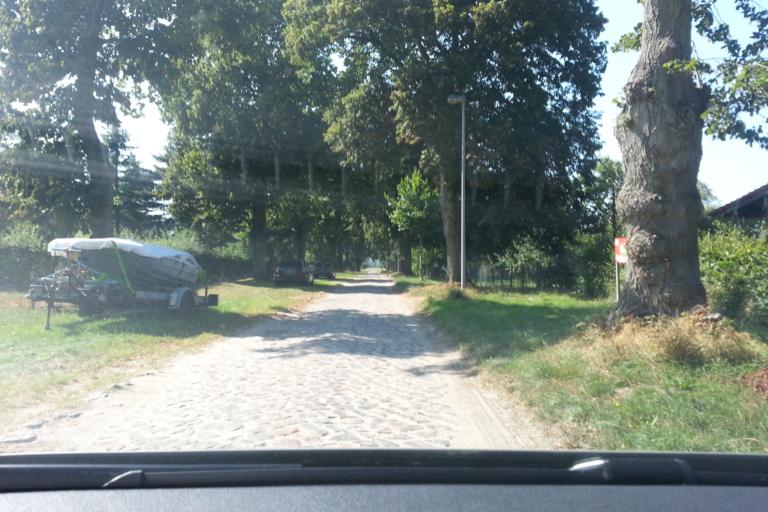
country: DE
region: Mecklenburg-Vorpommern
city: Ducherow
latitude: 53.7097
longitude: 13.7839
